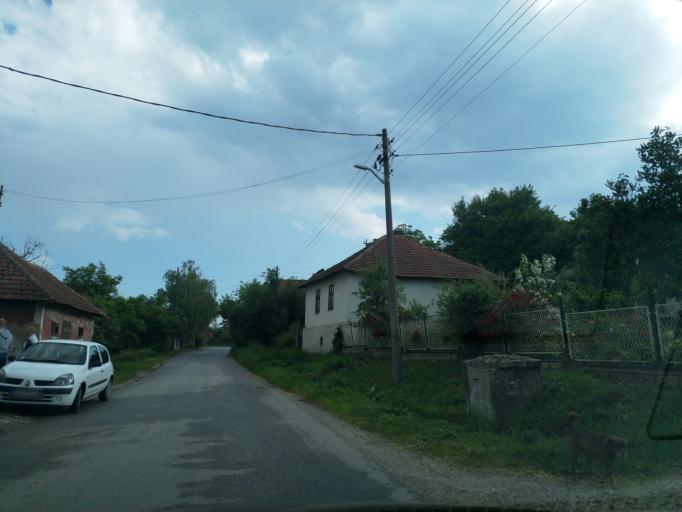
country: RS
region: Central Serbia
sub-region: Borski Okrug
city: Bor
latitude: 44.0077
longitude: 21.9847
